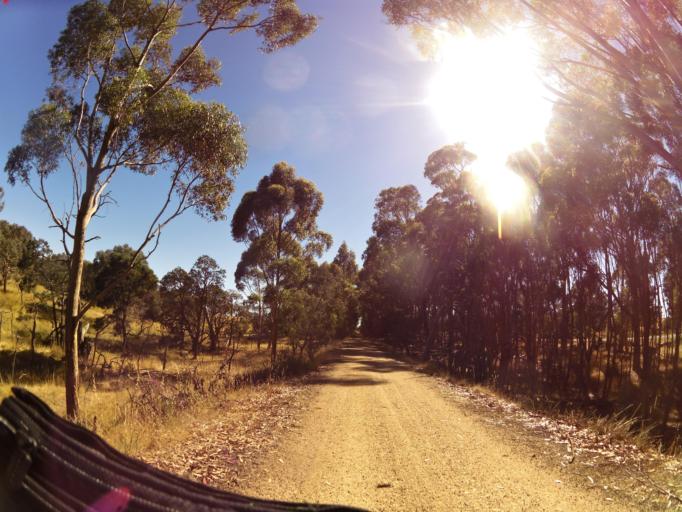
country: AU
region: Victoria
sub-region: Ballarat North
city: Delacombe
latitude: -37.6728
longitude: 143.4495
